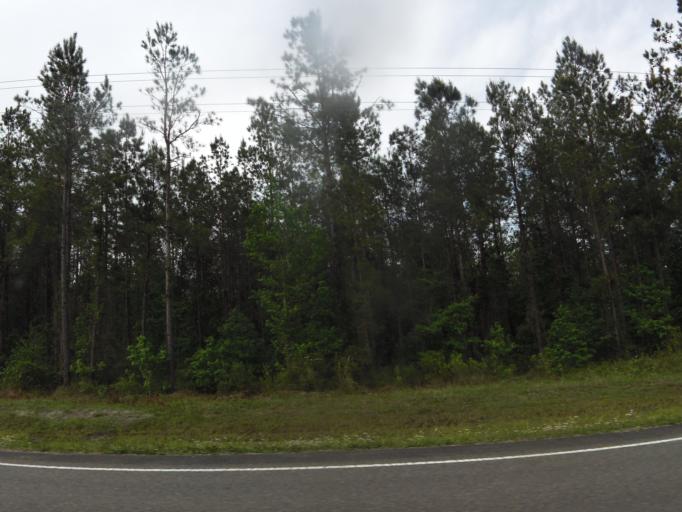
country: US
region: Florida
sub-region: Nassau County
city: Hilliard
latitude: 30.6946
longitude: -81.8440
